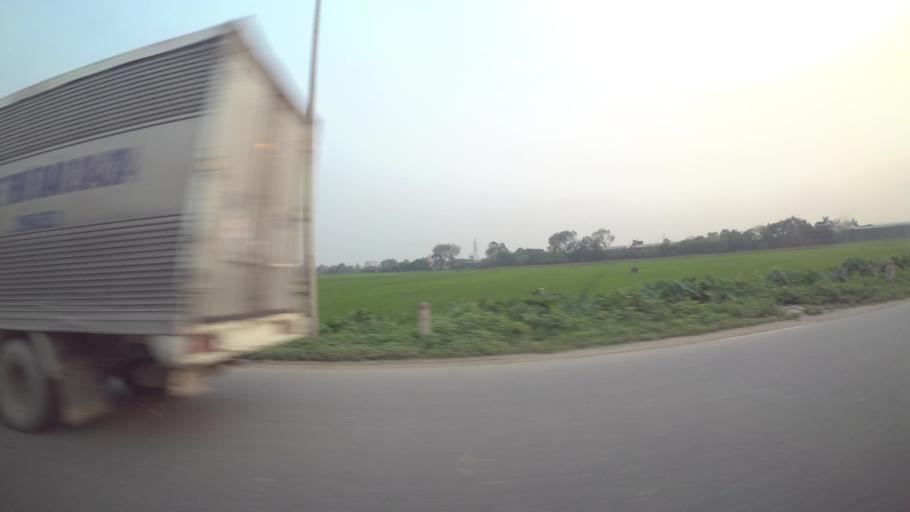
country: VN
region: Ha Noi
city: Thuong Tin
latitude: 20.8695
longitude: 105.8353
